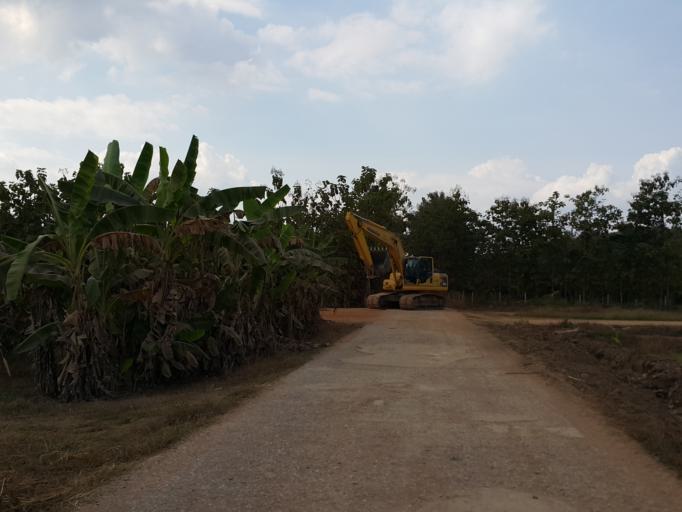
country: TH
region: Sukhothai
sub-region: Amphoe Si Satchanalai
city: Si Satchanalai
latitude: 17.4373
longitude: 99.6731
